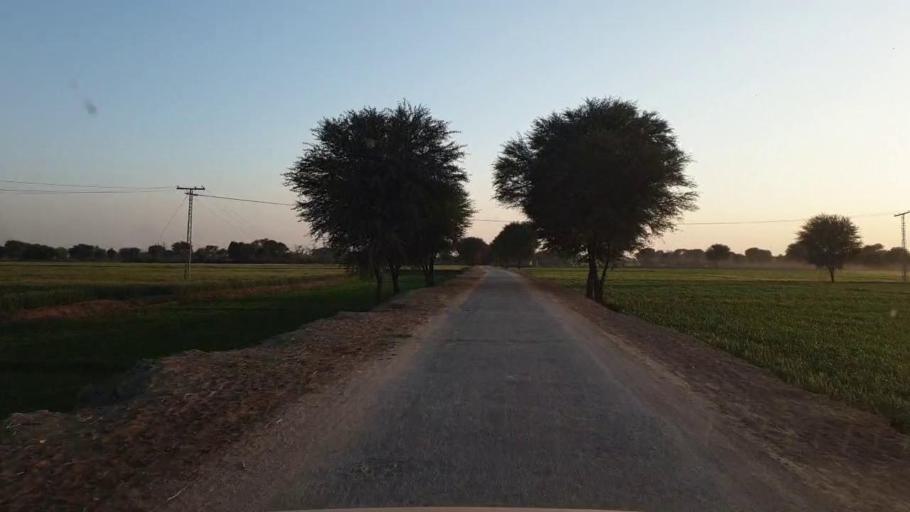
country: PK
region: Sindh
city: Tando Jam
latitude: 25.3063
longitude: 68.6383
